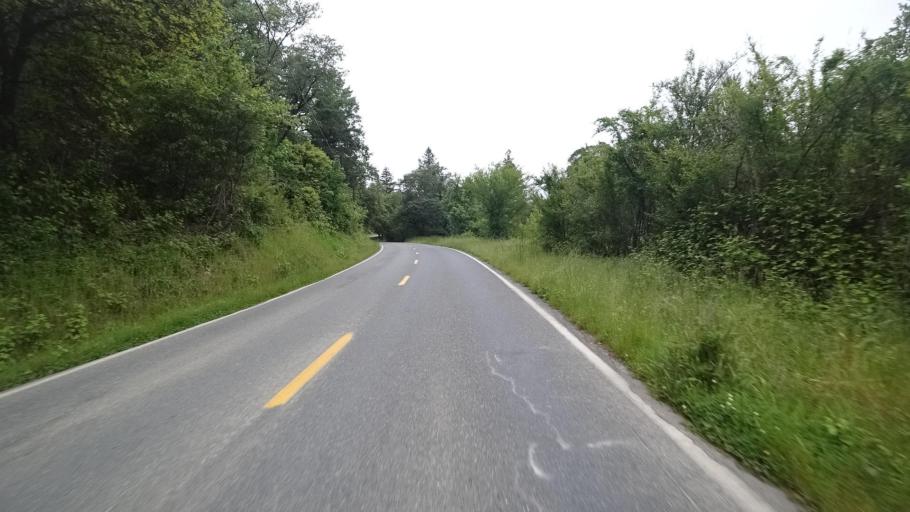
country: US
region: California
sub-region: Humboldt County
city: Willow Creek
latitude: 41.0697
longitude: -123.6943
